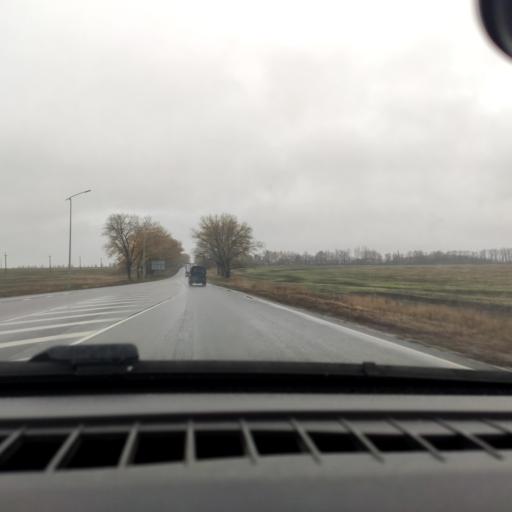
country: RU
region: Belgorod
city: Ilovka
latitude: 50.6884
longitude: 38.6610
